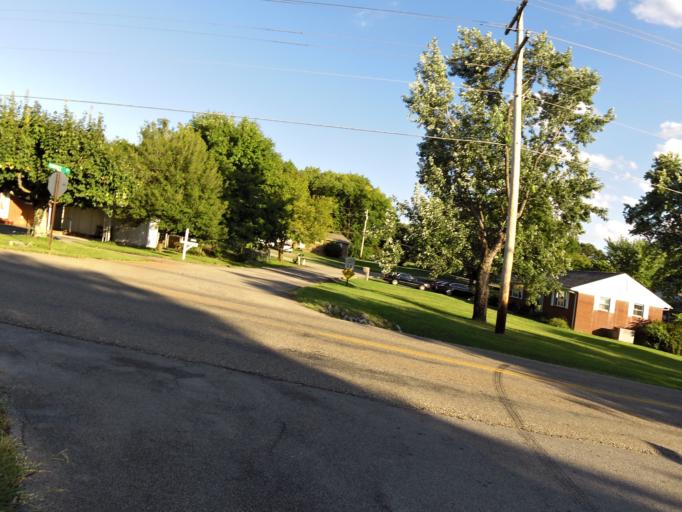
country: US
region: Tennessee
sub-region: Blount County
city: Eagleton Village
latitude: 35.7972
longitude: -83.9476
